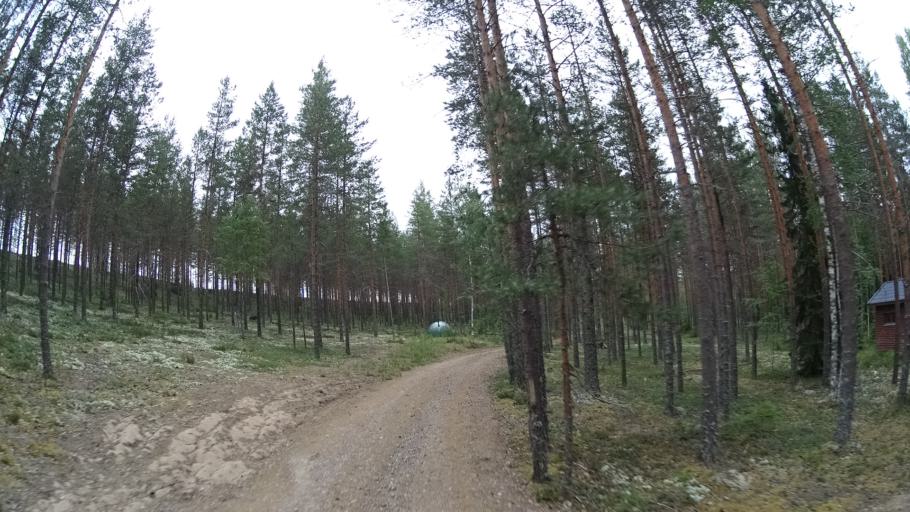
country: FI
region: Satakunta
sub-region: Pohjois-Satakunta
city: Jaemijaervi
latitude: 61.7684
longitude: 22.8151
